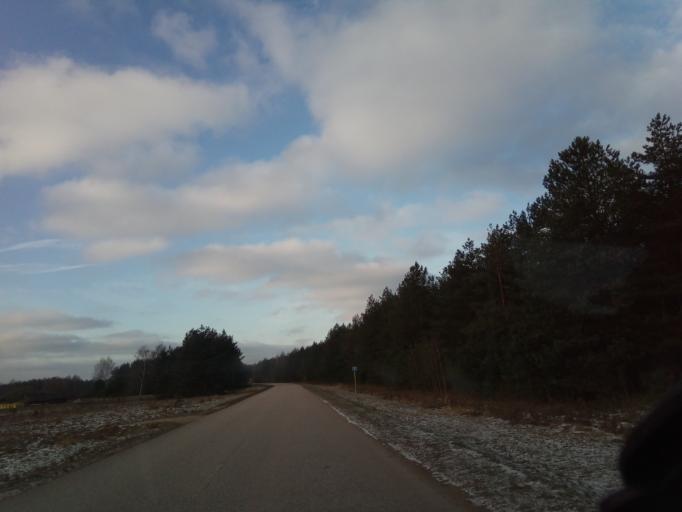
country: LT
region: Alytaus apskritis
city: Druskininkai
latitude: 53.9790
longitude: 24.2456
